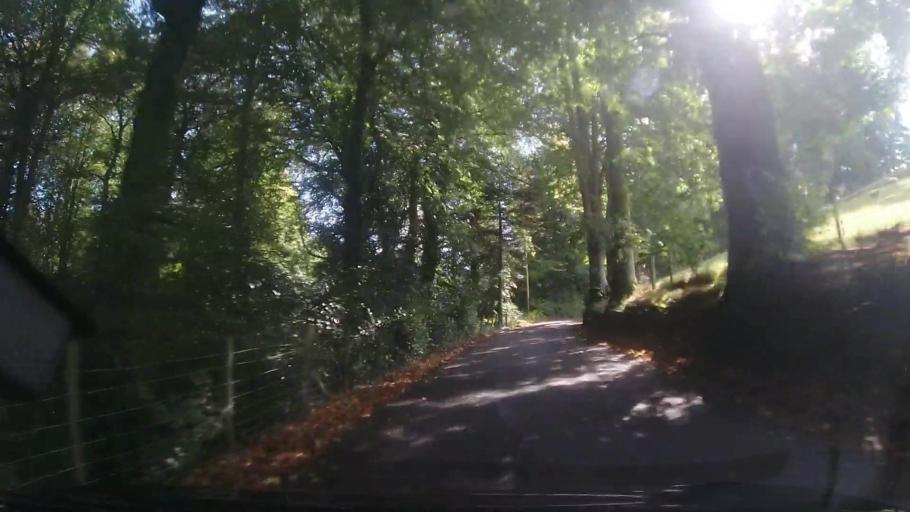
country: GB
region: Wales
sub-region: Gwynedd
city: Bala
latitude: 52.7620
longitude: -3.6216
